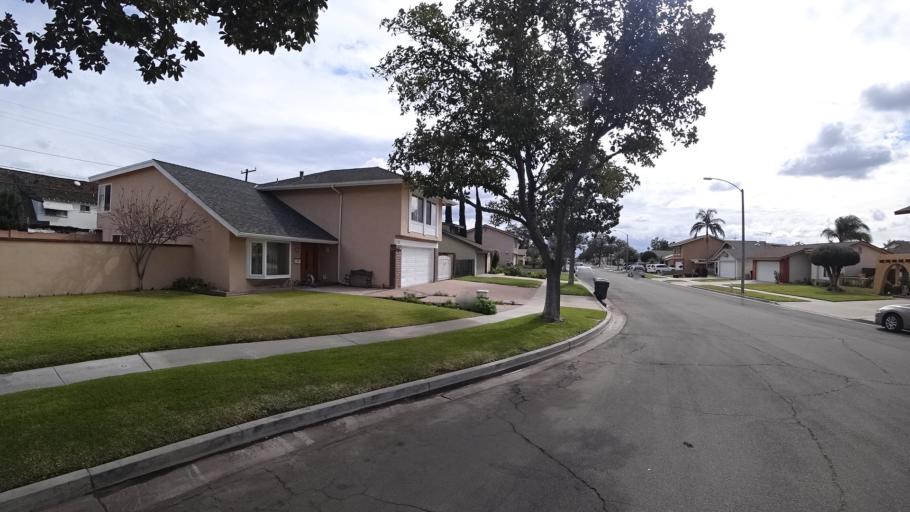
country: US
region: California
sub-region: Orange County
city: Placentia
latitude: 33.8401
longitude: -117.8677
